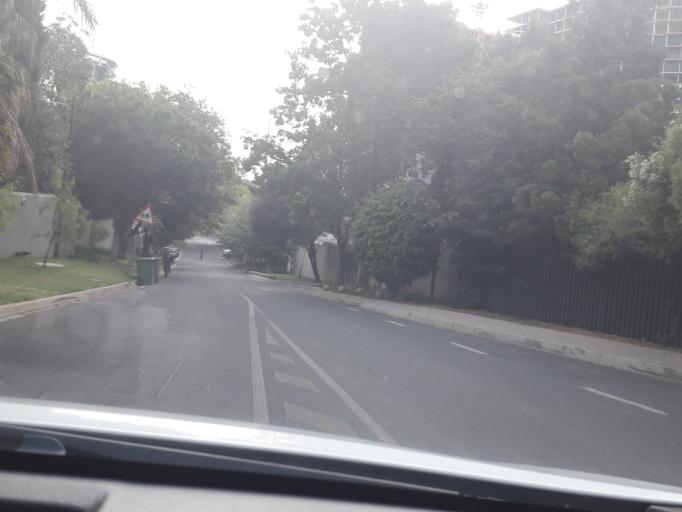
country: ZA
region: Gauteng
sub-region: City of Johannesburg Metropolitan Municipality
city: Johannesburg
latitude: -26.0981
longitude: 28.0526
